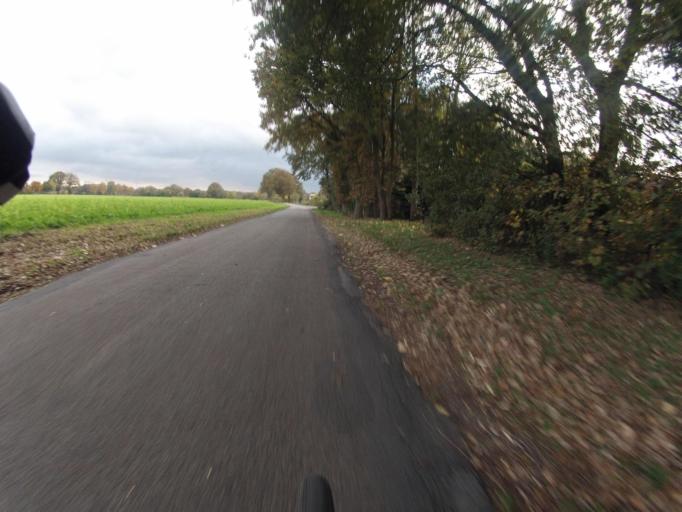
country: DE
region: North Rhine-Westphalia
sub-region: Regierungsbezirk Munster
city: Horstel
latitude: 52.2681
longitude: 7.5705
